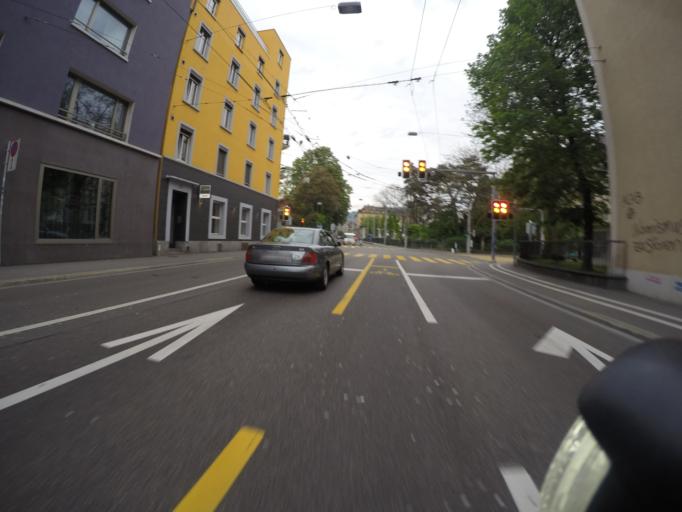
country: CH
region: Zurich
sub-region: Bezirk Zuerich
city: Aussersihl
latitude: 47.3789
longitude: 8.5234
